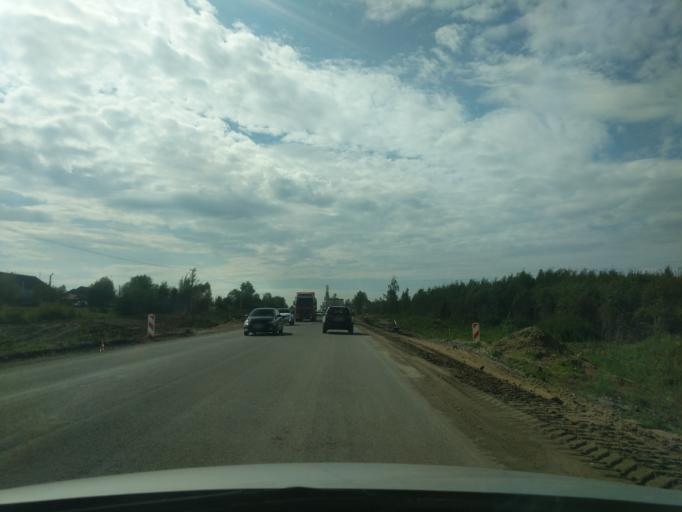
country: RU
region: Kostroma
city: Sudislavl'
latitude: 57.8654
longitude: 41.6292
